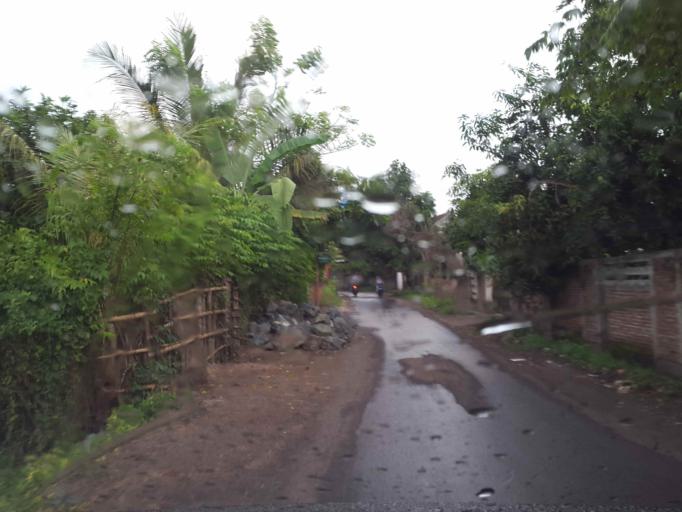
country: ID
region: West Nusa Tenggara
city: Kekeri
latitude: -8.5574
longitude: 116.1256
